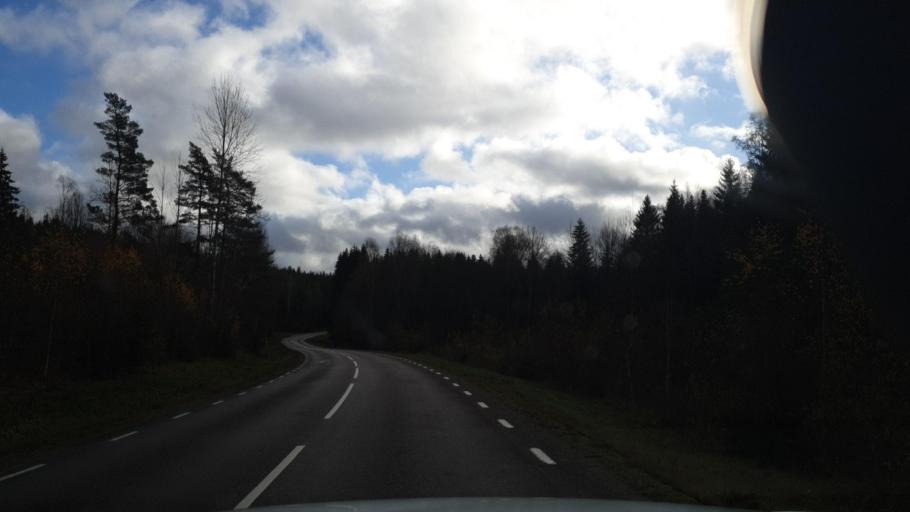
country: SE
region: Vaermland
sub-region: Grums Kommun
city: Slottsbron
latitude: 59.4509
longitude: 12.8463
